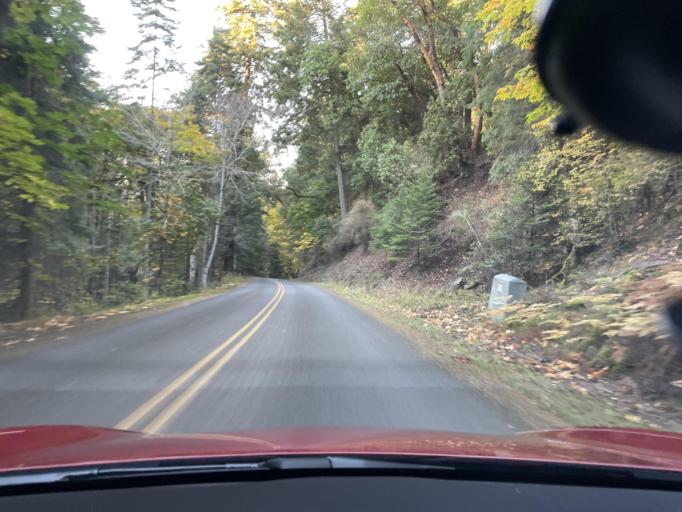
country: US
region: Washington
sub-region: San Juan County
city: Friday Harbor
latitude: 48.5380
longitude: -123.1581
